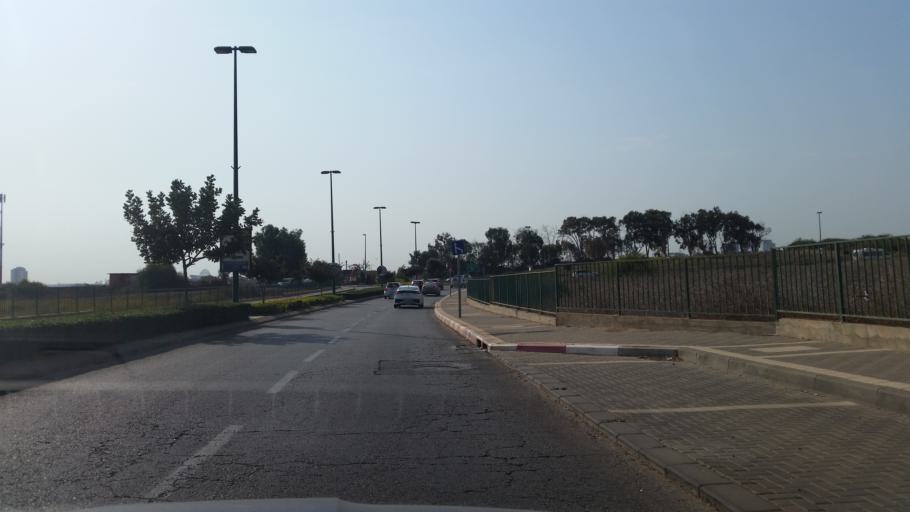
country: IL
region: Central District
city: Netanya
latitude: 32.3097
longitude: 34.8613
